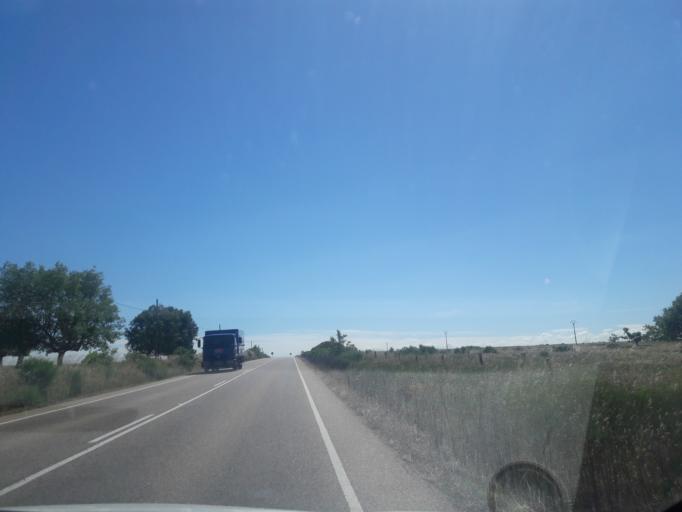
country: ES
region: Castille and Leon
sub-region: Provincia de Salamanca
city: Cerralbo
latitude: 40.9689
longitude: -6.6217
